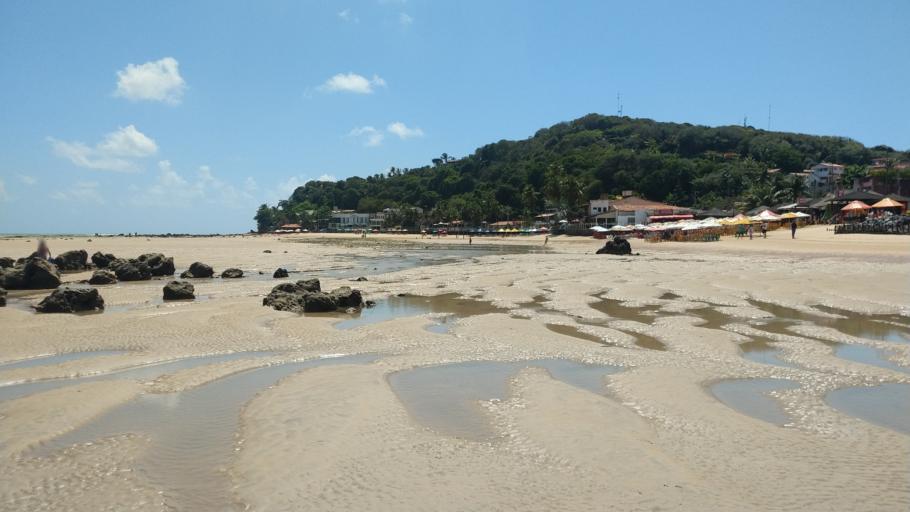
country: BR
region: Rio Grande do Norte
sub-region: Ares
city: Ares
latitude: -6.2273
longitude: -35.0487
